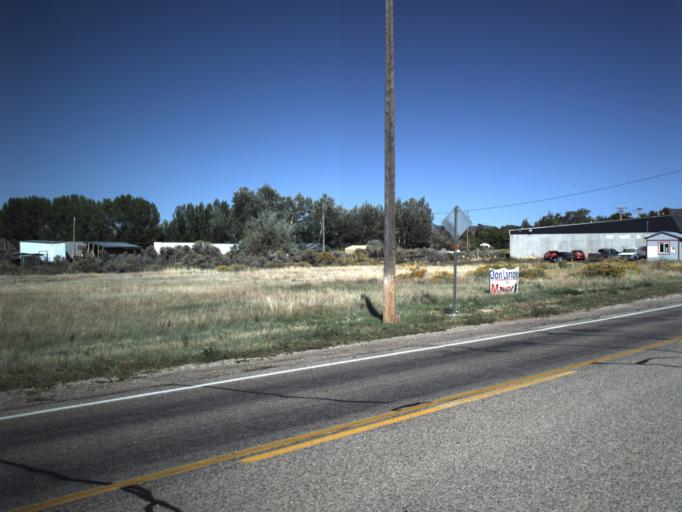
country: US
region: Utah
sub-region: Iron County
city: Parowan
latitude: 37.8387
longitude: -112.8431
